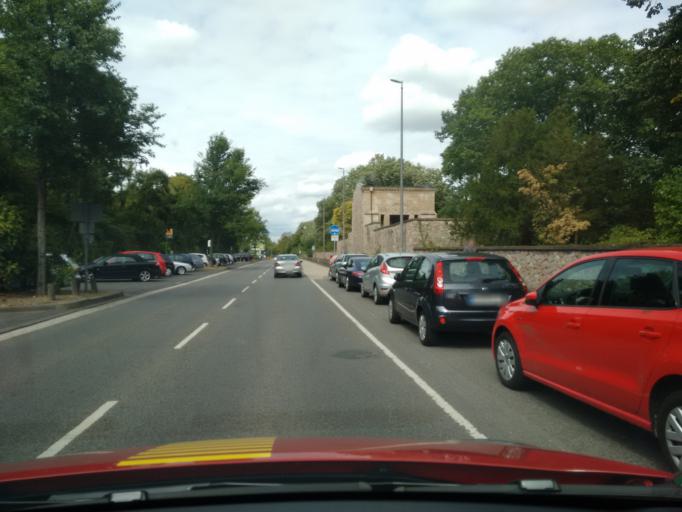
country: DE
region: Rheinland-Pfalz
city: Mainz
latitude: 49.9940
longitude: 8.2466
